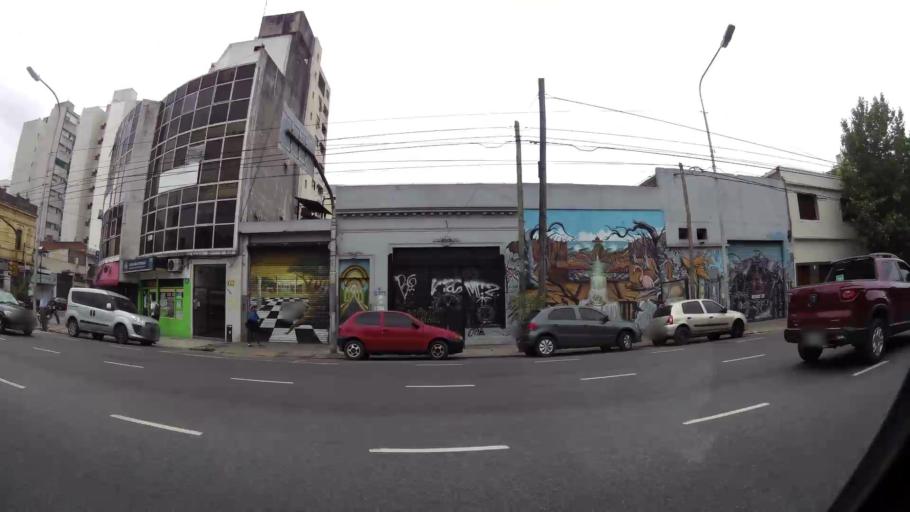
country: AR
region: Buenos Aires
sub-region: Partido de Avellaneda
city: Avellaneda
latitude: -34.6671
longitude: -58.3648
